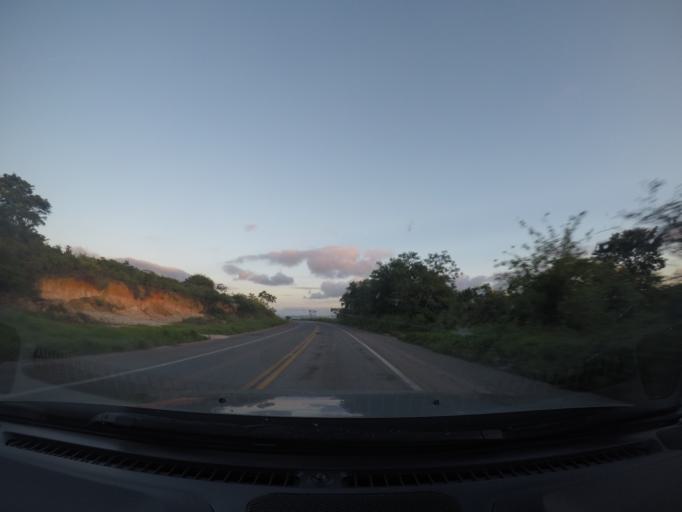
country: BR
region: Bahia
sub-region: Seabra
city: Seabra
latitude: -12.4330
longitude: -41.8235
